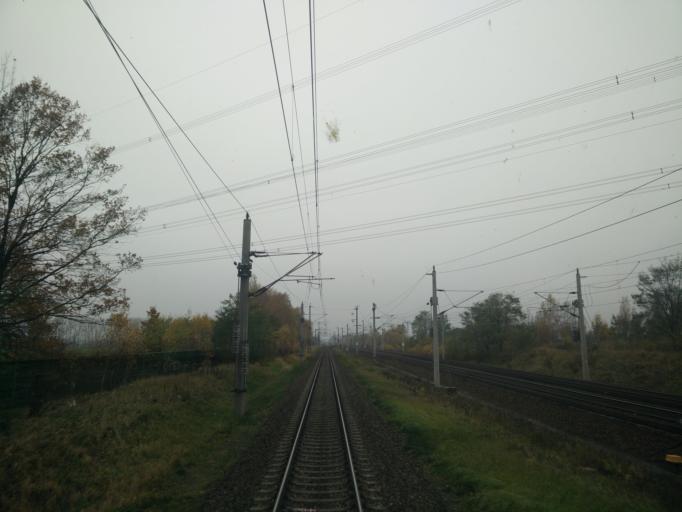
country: DE
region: Brandenburg
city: Wustermark
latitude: 52.5525
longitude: 12.9310
